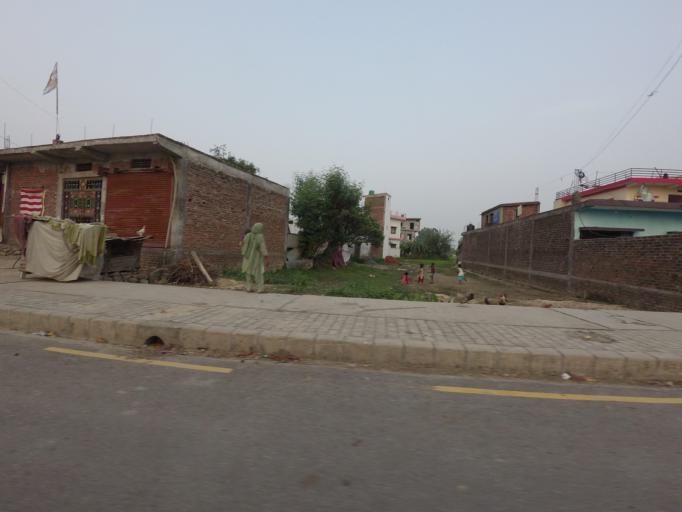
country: NP
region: Western Region
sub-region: Lumbini Zone
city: Bhairahawa
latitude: 27.5005
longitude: 83.4632
